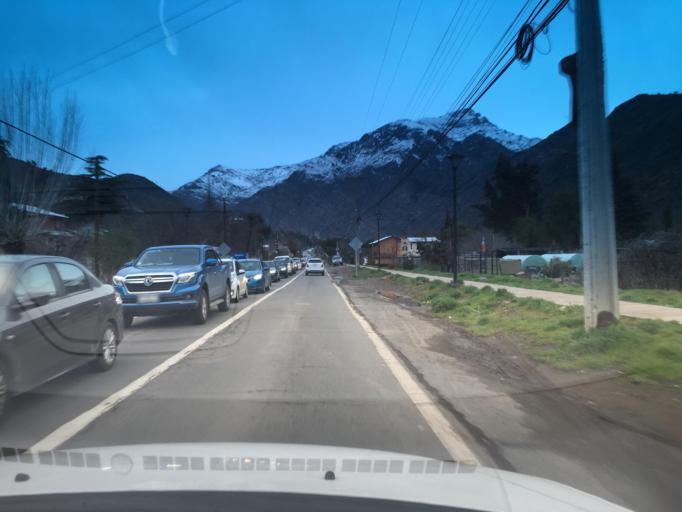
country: CL
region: Santiago Metropolitan
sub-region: Provincia de Cordillera
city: Puente Alto
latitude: -33.6969
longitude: -70.3347
